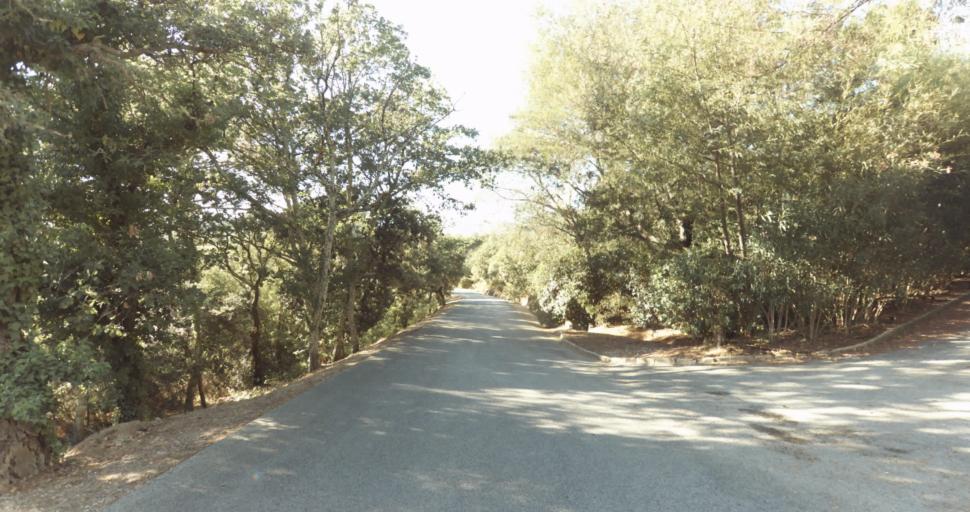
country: FR
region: Provence-Alpes-Cote d'Azur
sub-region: Departement du Var
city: Gassin
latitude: 43.2374
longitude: 6.5972
